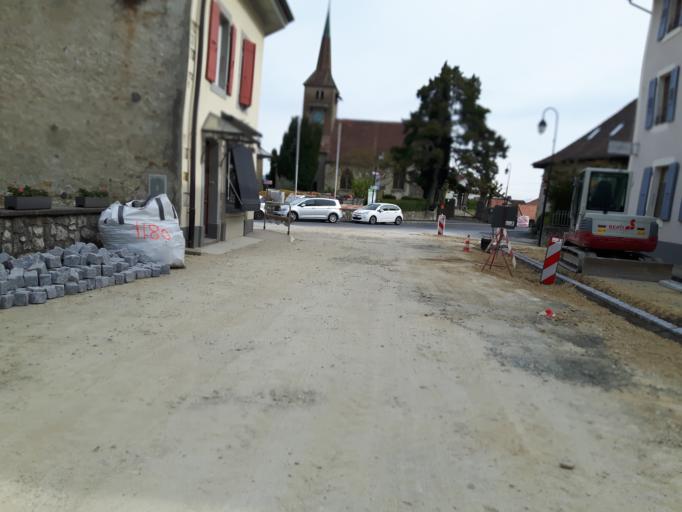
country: CH
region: Vaud
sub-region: Jura-Nord vaudois District
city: Yvonand
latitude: 46.8506
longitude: 6.7197
